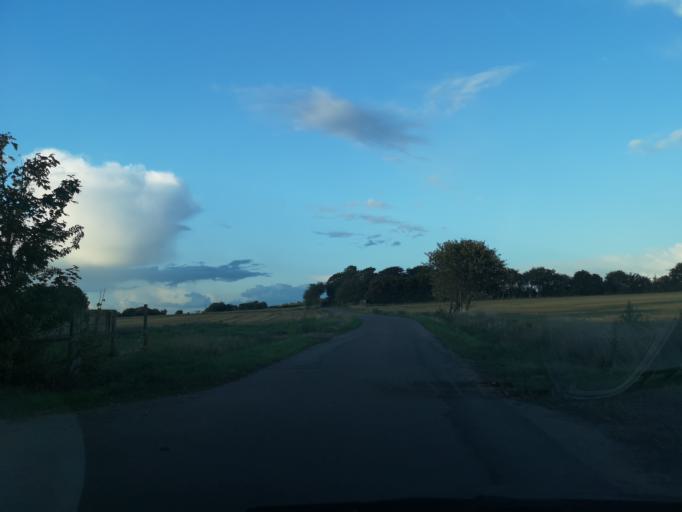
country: DK
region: Central Jutland
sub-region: Ringkobing-Skjern Kommune
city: Videbaek
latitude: 56.0284
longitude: 8.5656
